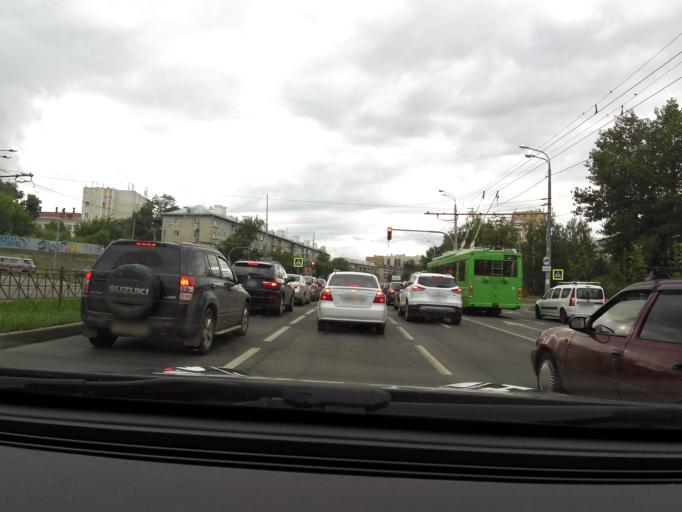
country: RU
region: Tatarstan
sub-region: Gorod Kazan'
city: Kazan
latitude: 55.8182
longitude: 49.0594
